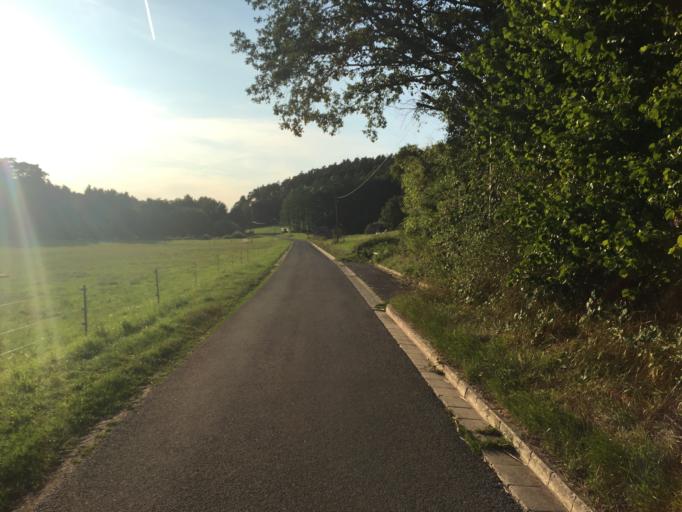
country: DE
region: Bavaria
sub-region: Regierungsbezirk Mittelfranken
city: Wilhermsdorf
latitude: 49.4923
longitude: 10.6983
